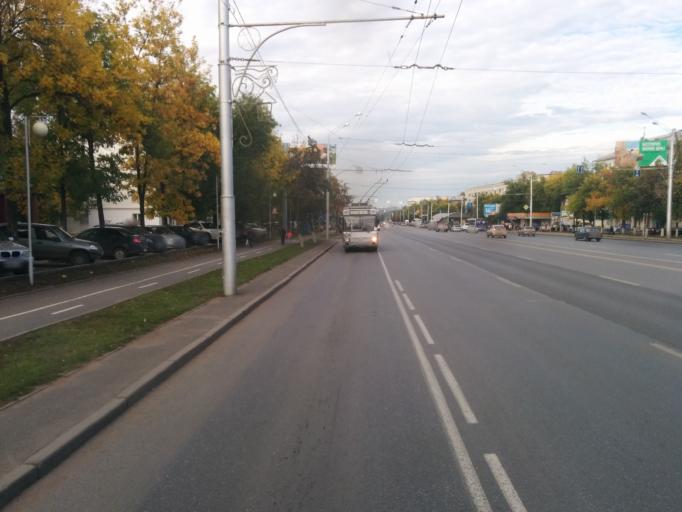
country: RU
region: Bashkortostan
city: Ufa
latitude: 54.7879
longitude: 56.0349
